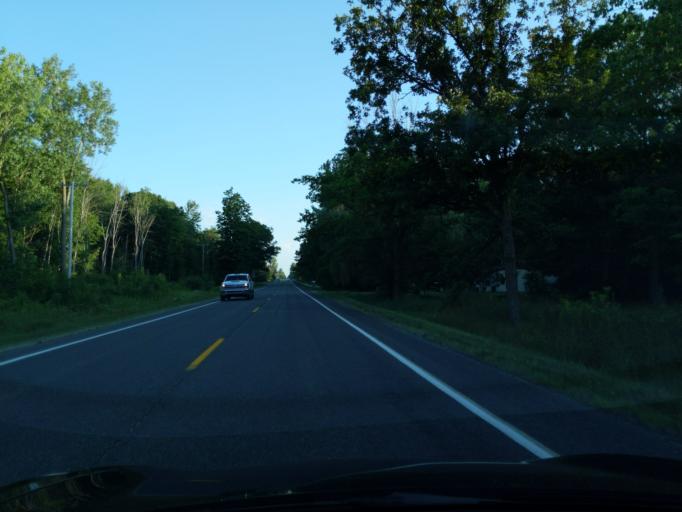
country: US
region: Michigan
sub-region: Midland County
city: Midland
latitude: 43.5564
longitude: -84.3697
